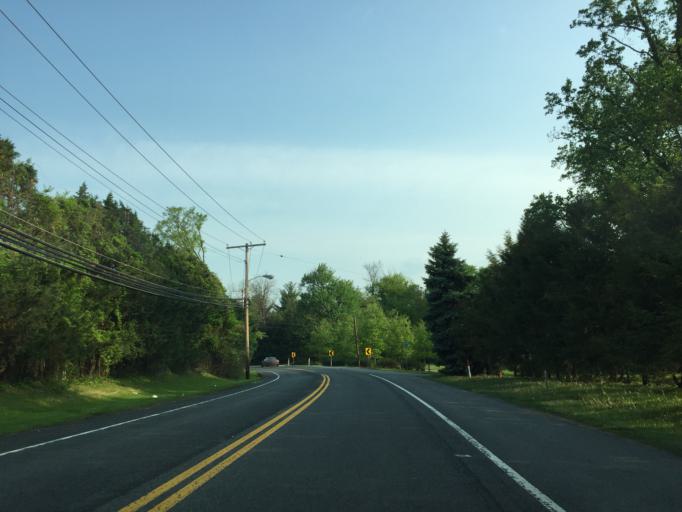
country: US
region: Maryland
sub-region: Baltimore County
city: Pikesville
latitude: 39.3768
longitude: -76.7129
